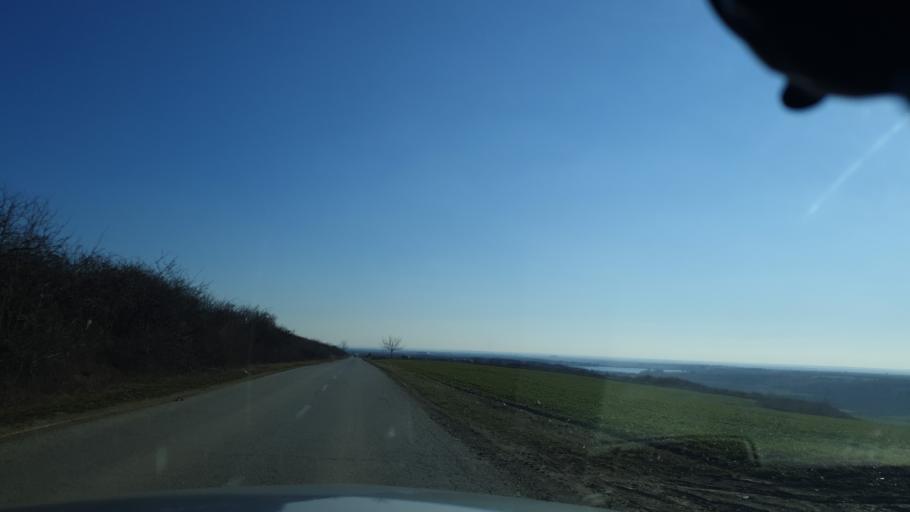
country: RS
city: Vrdnik
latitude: 45.0936
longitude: 19.8055
